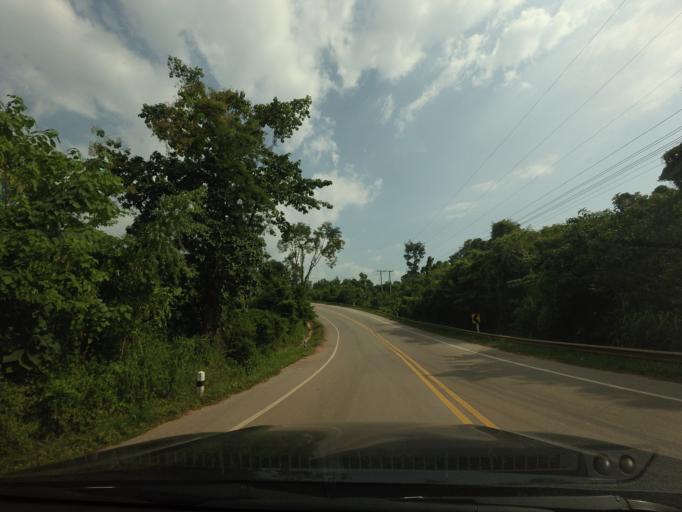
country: TH
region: Phitsanulok
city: Nakhon Thai
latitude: 17.0178
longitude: 100.9157
